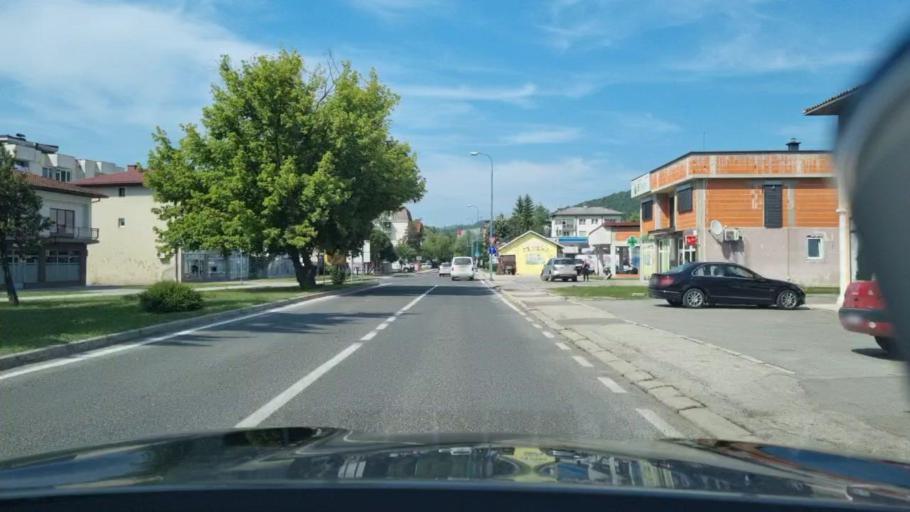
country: BA
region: Federation of Bosnia and Herzegovina
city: Bosanska Krupa
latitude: 44.8793
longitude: 16.1524
